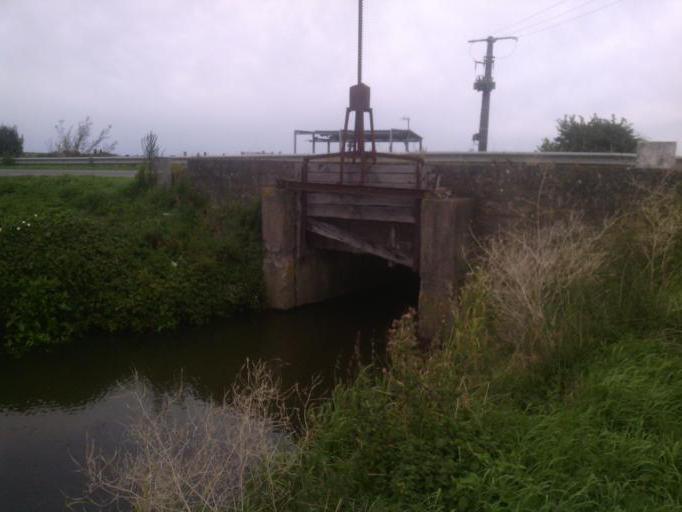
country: FR
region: Nord-Pas-de-Calais
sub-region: Departement du Nord
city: Killem
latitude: 50.9885
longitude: 2.5418
